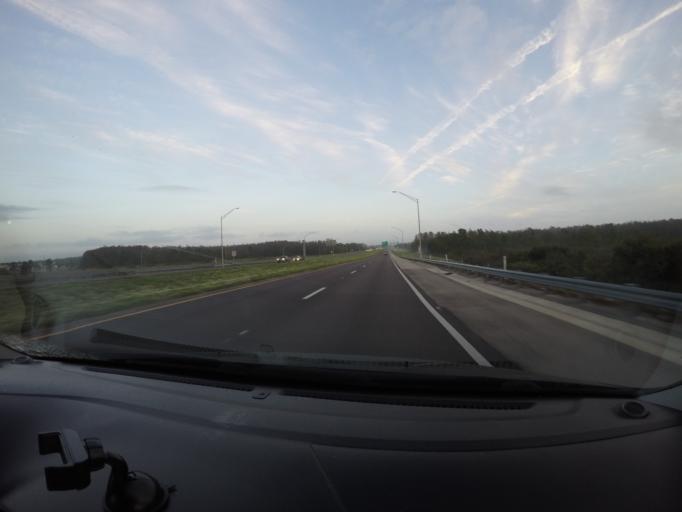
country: US
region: Florida
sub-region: Orange County
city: Conway
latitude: 28.4305
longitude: -81.2285
